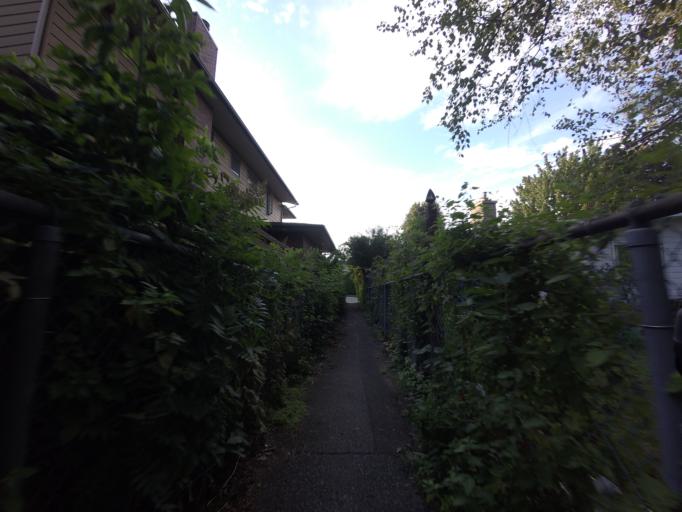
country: CA
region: Ontario
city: Bells Corners
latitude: 45.2789
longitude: -75.7709
